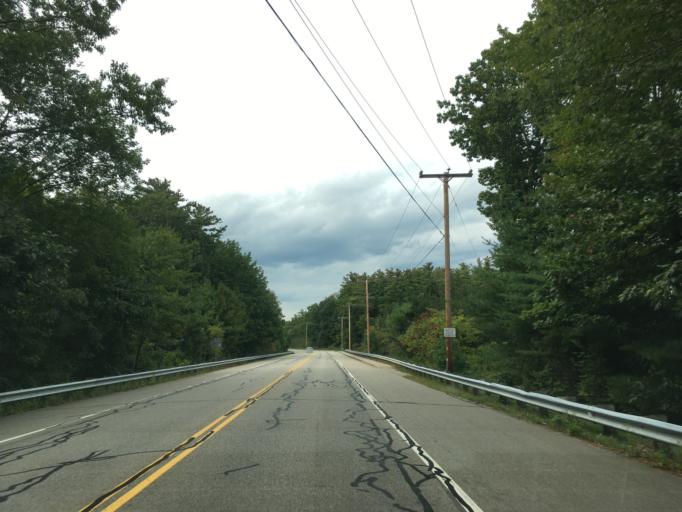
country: US
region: New Hampshire
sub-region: Rockingham County
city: Exeter
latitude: 42.9816
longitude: -70.9193
